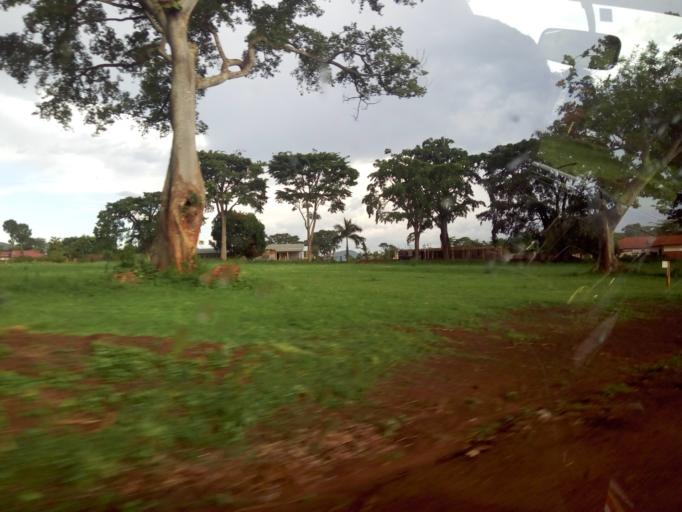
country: UG
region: Western Region
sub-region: Masindi District
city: Masindi
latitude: 1.6880
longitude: 31.7169
